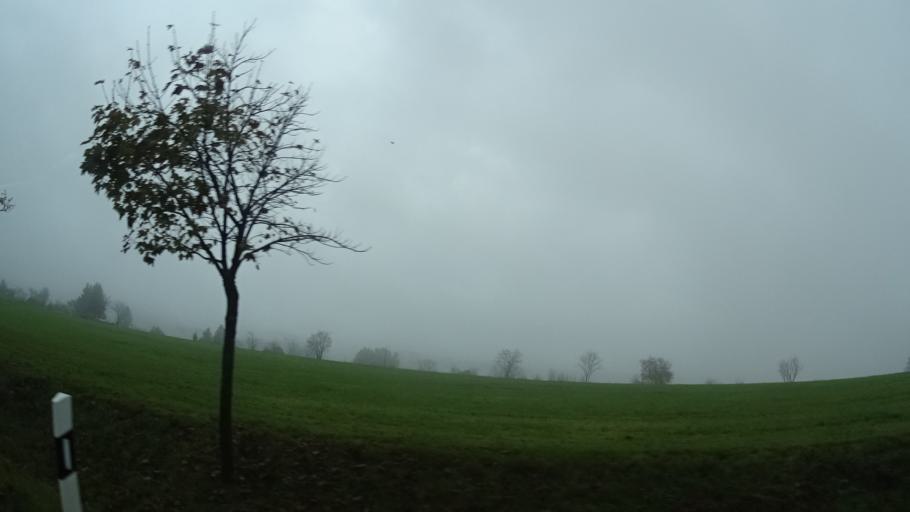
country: DE
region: Bavaria
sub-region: Upper Franconia
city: Tschirn
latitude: 50.4044
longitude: 11.4482
